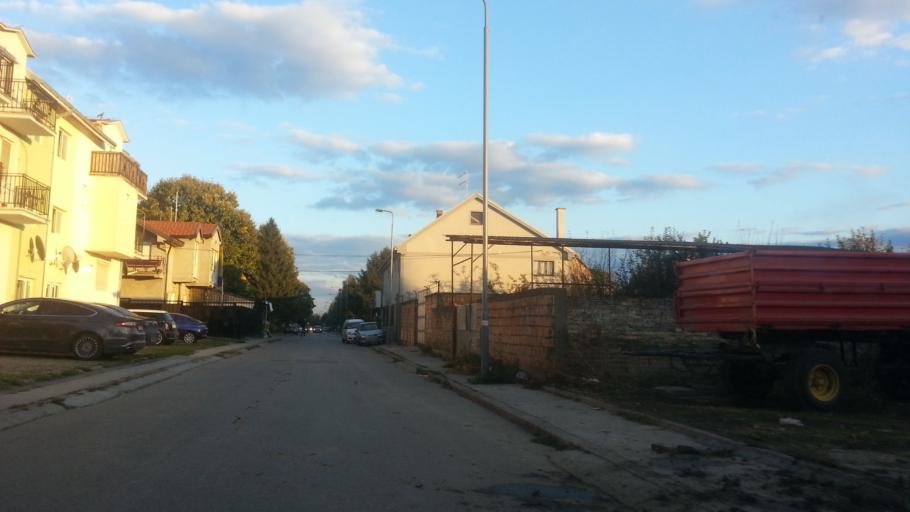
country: RS
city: Novi Banovci
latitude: 44.9034
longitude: 20.2817
